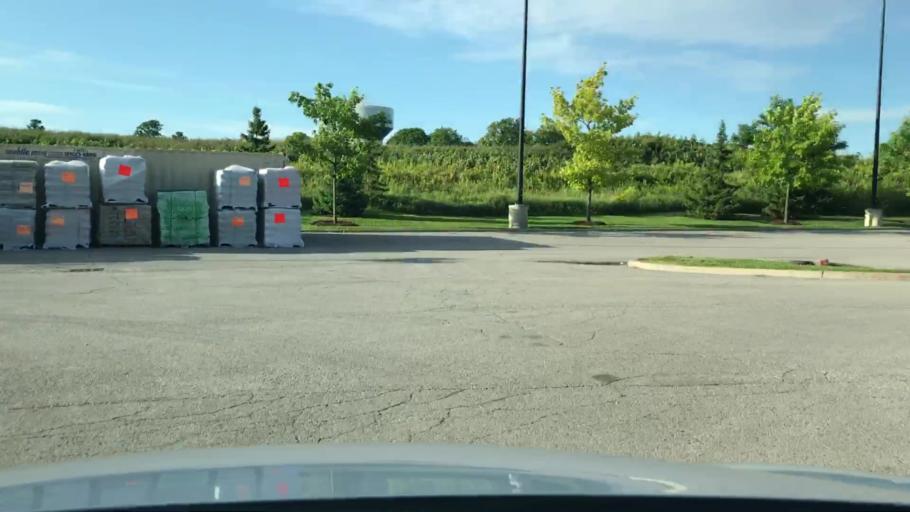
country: CA
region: Ontario
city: Newmarket
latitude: 44.0152
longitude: -79.4159
